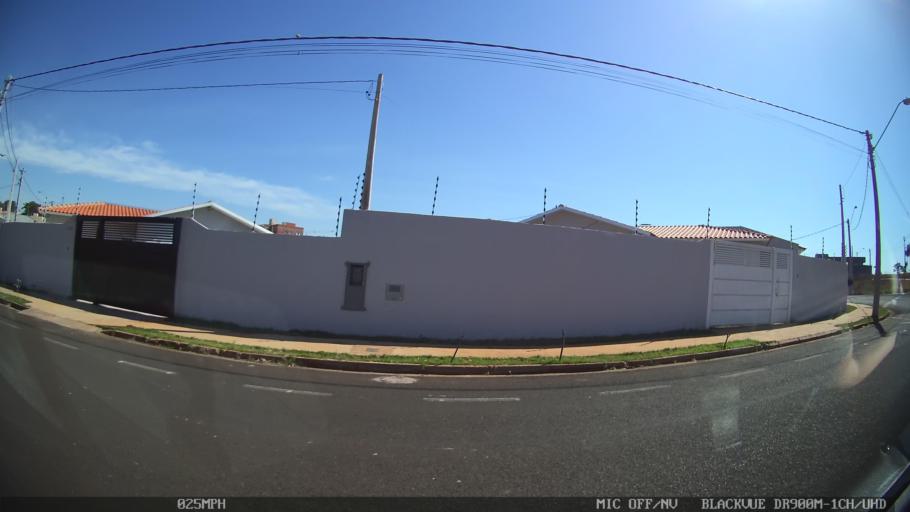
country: BR
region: Sao Paulo
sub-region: Sao Jose Do Rio Preto
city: Sao Jose do Rio Preto
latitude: -20.7517
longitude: -49.4224
